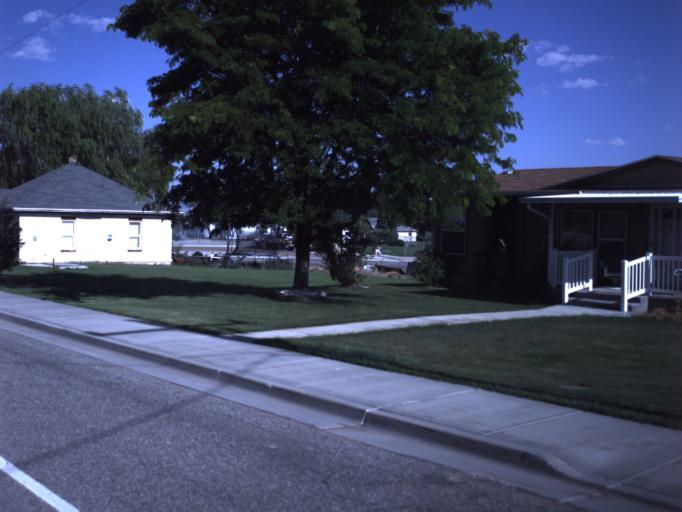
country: US
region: Utah
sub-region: Emery County
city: Huntington
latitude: 39.3486
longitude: -110.8588
